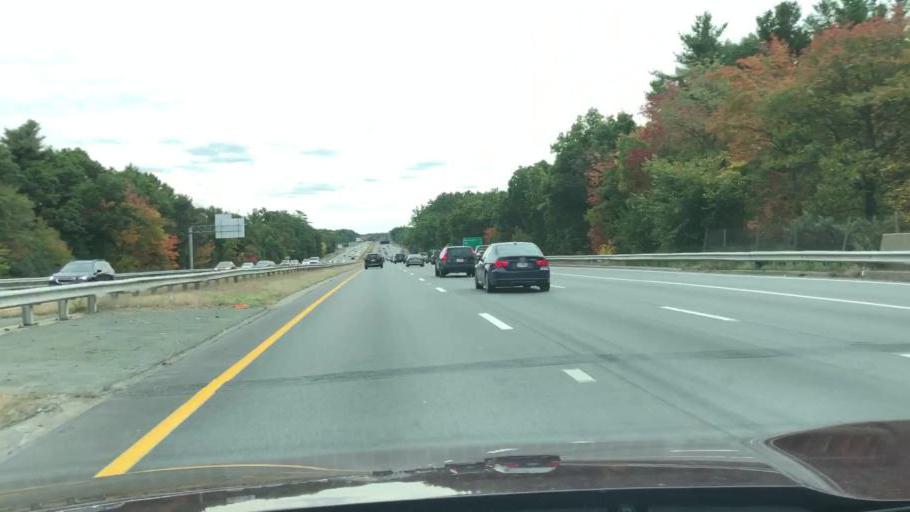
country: US
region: Massachusetts
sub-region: Essex County
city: Andover
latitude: 42.6170
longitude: -71.1756
